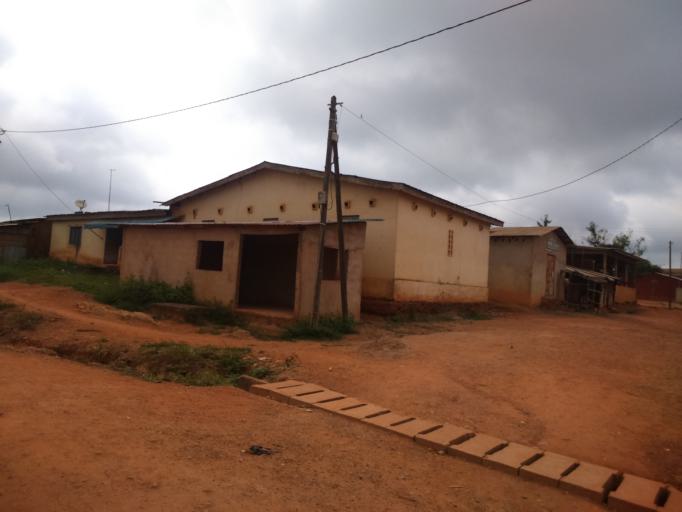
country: CI
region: Agneby
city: Agboville
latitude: 6.0134
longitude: -4.1447
